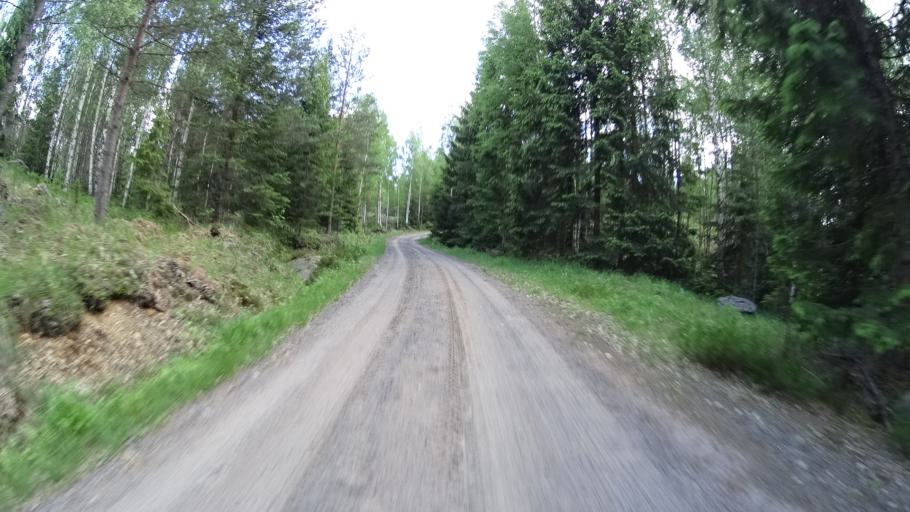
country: FI
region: Varsinais-Suomi
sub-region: Salo
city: Kisko
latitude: 60.1887
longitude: 23.5522
